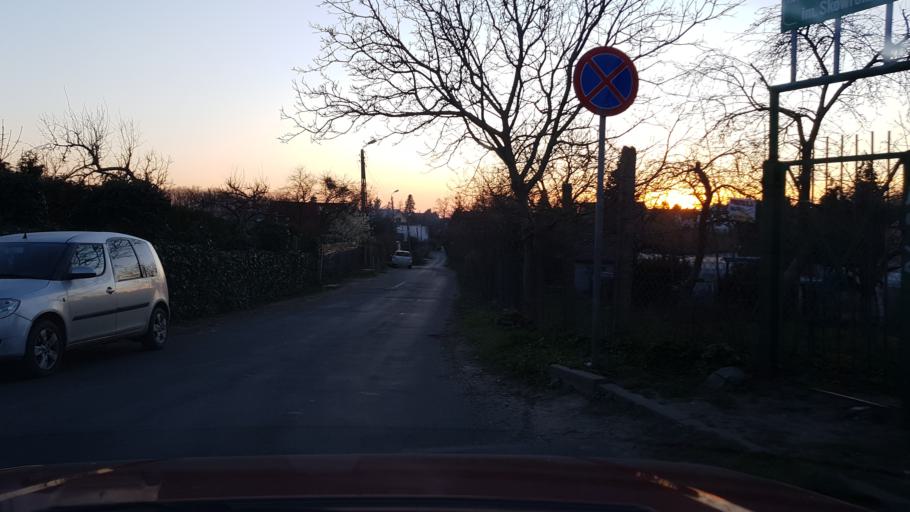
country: PL
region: West Pomeranian Voivodeship
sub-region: Szczecin
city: Szczecin
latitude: 53.4664
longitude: 14.5524
